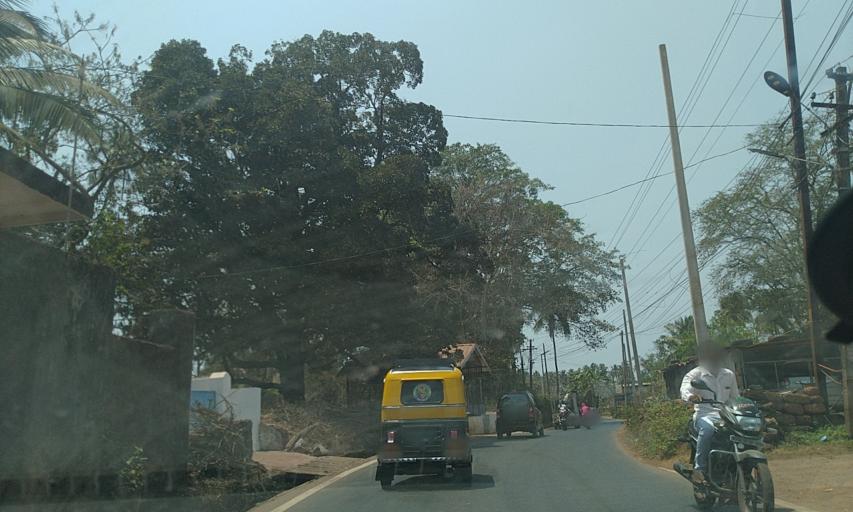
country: IN
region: Goa
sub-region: North Goa
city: Vagator
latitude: 15.5903
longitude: 73.7678
